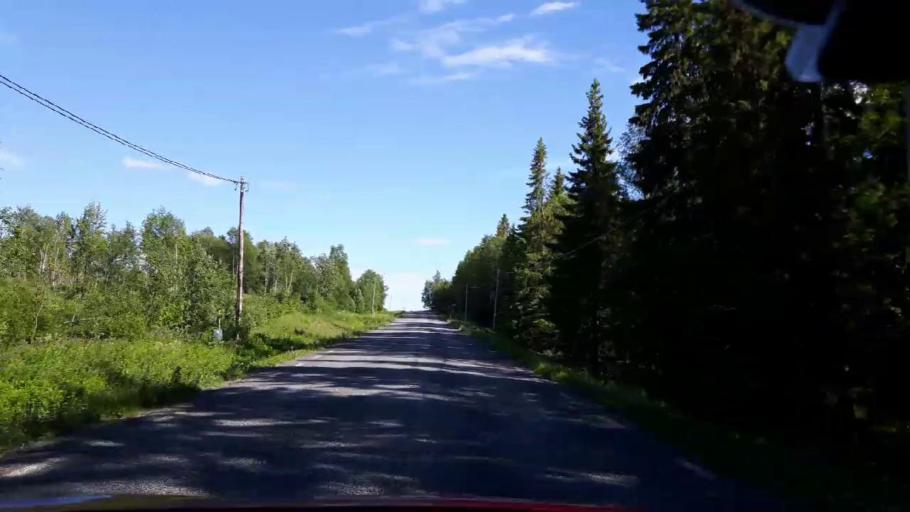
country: SE
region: Jaemtland
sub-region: Krokoms Kommun
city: Valla
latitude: 63.7010
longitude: 14.1509
